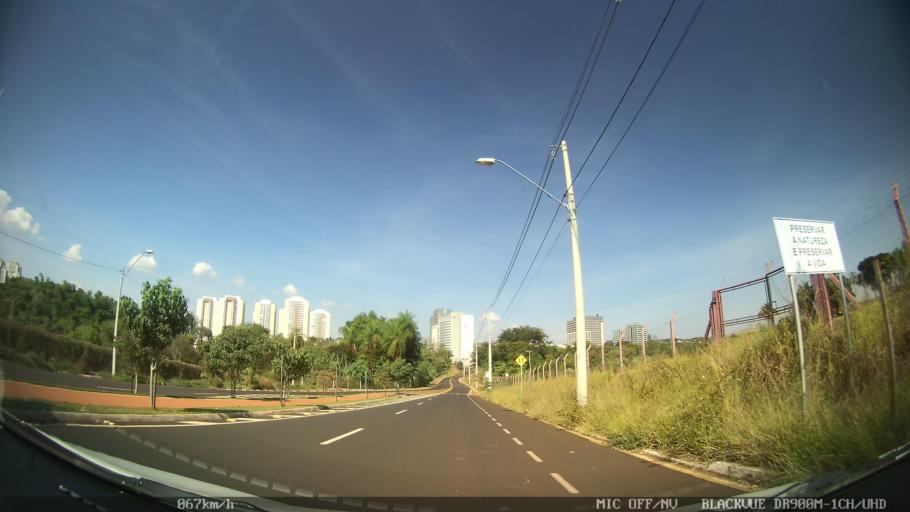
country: BR
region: Sao Paulo
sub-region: Ribeirao Preto
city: Ribeirao Preto
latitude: -21.2198
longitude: -47.8375
